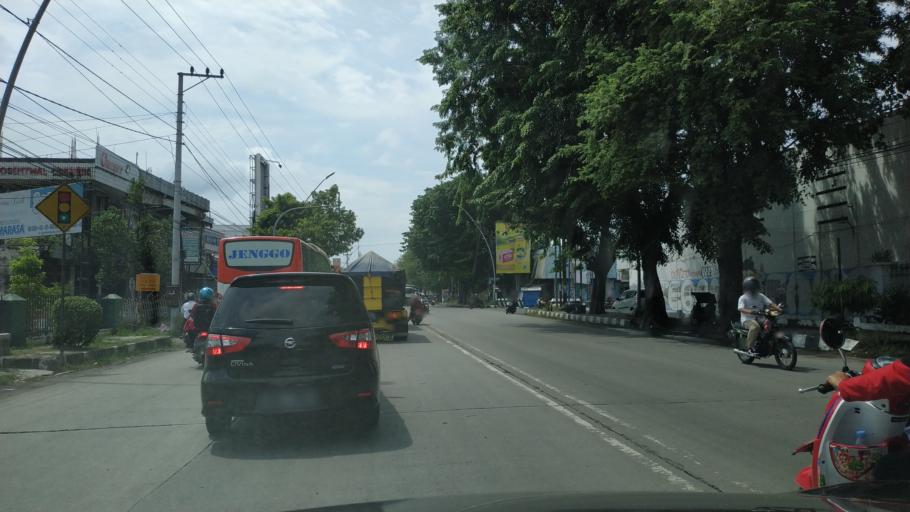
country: ID
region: Central Java
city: Tegal
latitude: -6.8669
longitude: 109.1335
